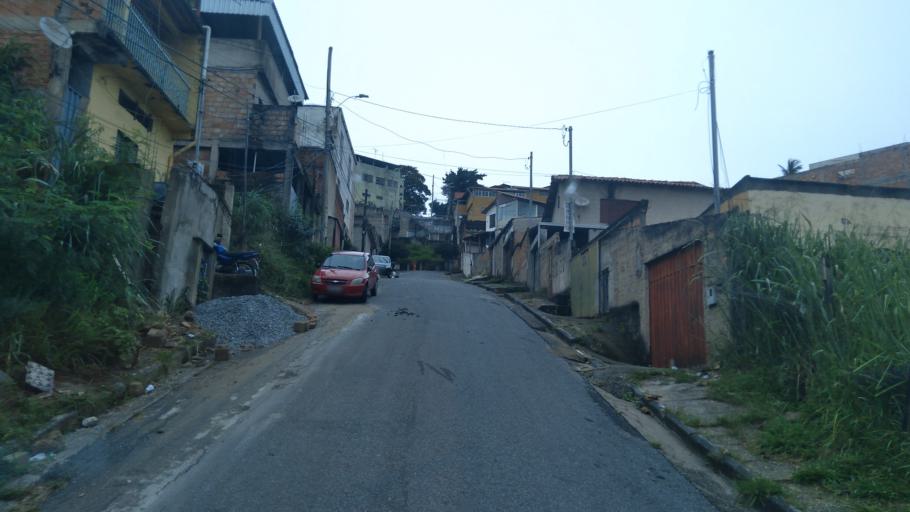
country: BR
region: Minas Gerais
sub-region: Belo Horizonte
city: Belo Horizonte
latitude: -19.9145
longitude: -43.8843
